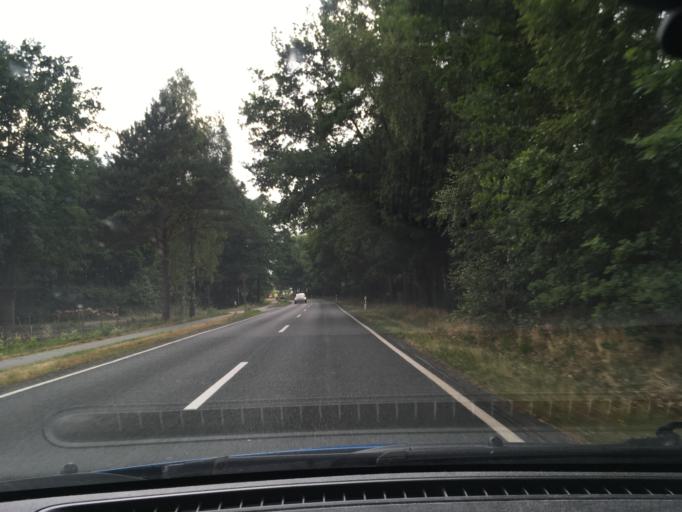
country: DE
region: Lower Saxony
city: Hollenstedt
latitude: 53.3588
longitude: 9.7302
